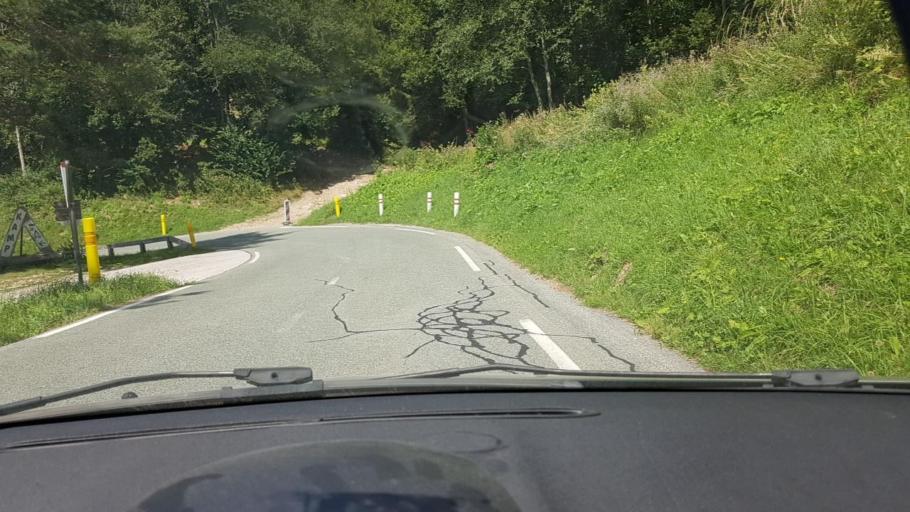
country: SI
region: Jezersko
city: Zgornje Jezersko
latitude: 46.4095
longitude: 14.5226
